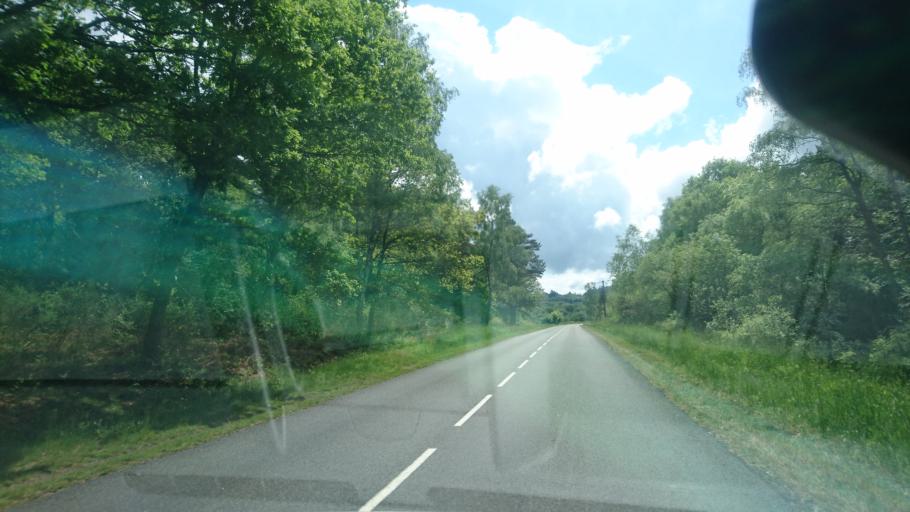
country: FR
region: Limousin
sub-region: Departement de la Haute-Vienne
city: Peyrat-le-Chateau
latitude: 45.7811
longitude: 1.8623
